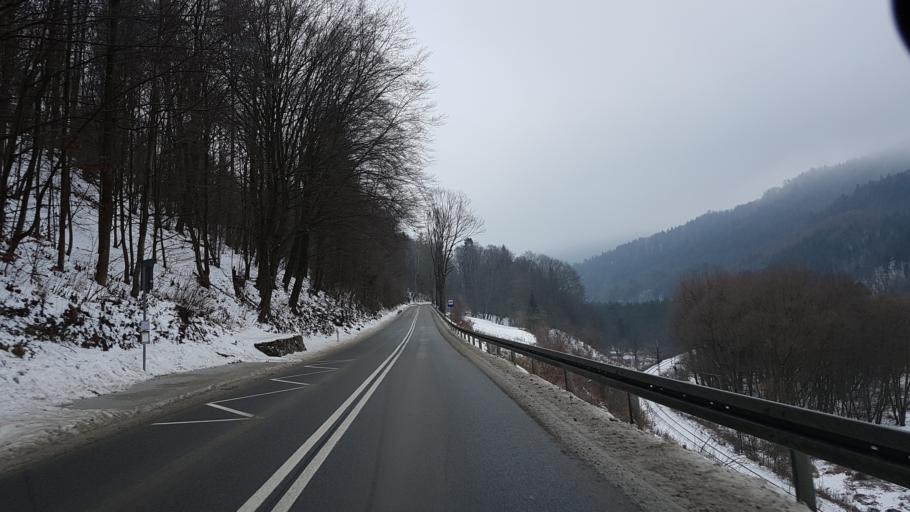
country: PL
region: Lesser Poland Voivodeship
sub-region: Powiat nowosadecki
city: Piwniczna-Zdroj
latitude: 49.4103
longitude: 20.7470
